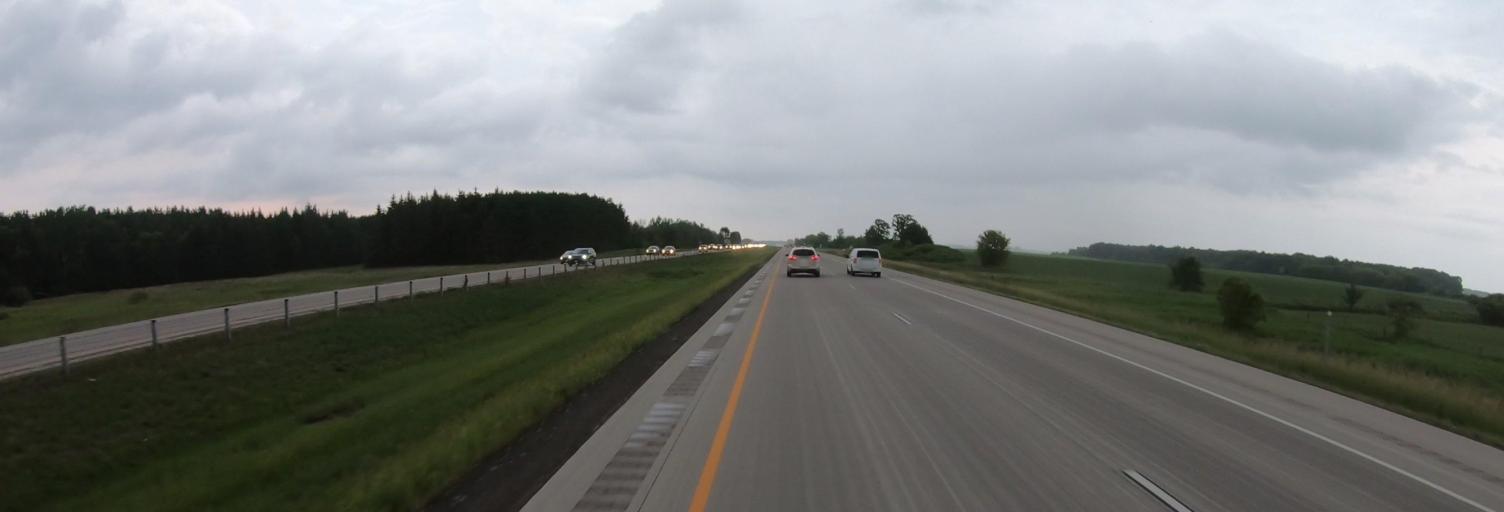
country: US
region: Minnesota
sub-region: Pine County
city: Rock Creek
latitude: 45.7254
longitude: -92.9918
